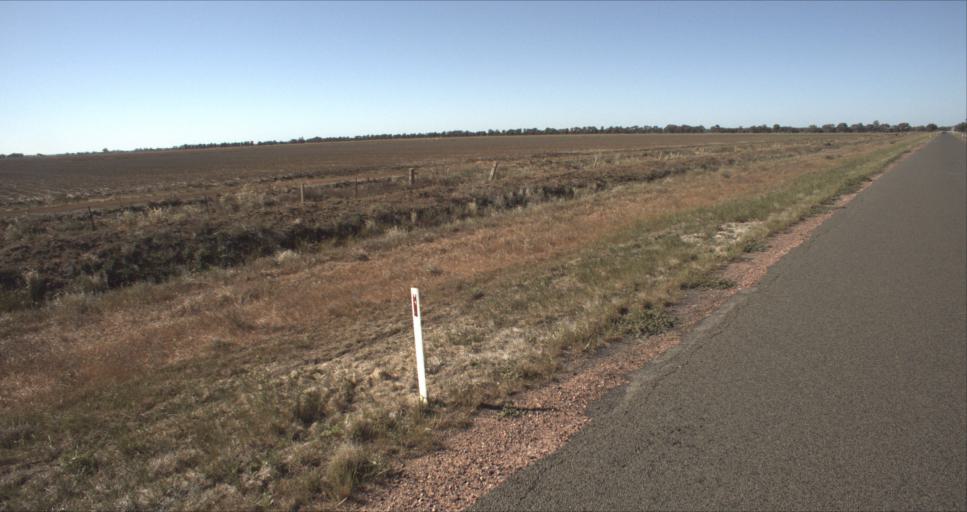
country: AU
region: New South Wales
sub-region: Leeton
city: Leeton
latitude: -34.5682
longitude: 146.2640
